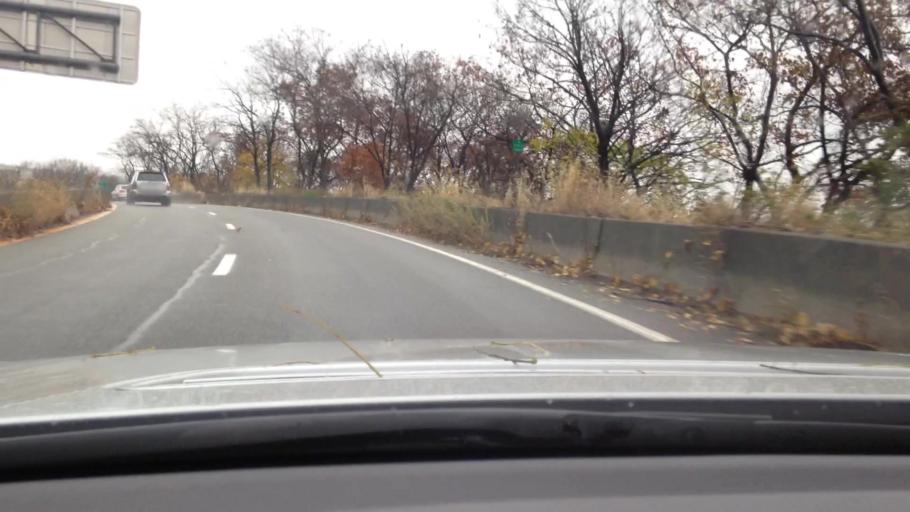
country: US
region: New York
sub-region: Westchester County
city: Peekskill
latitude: 41.2929
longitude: -73.9347
